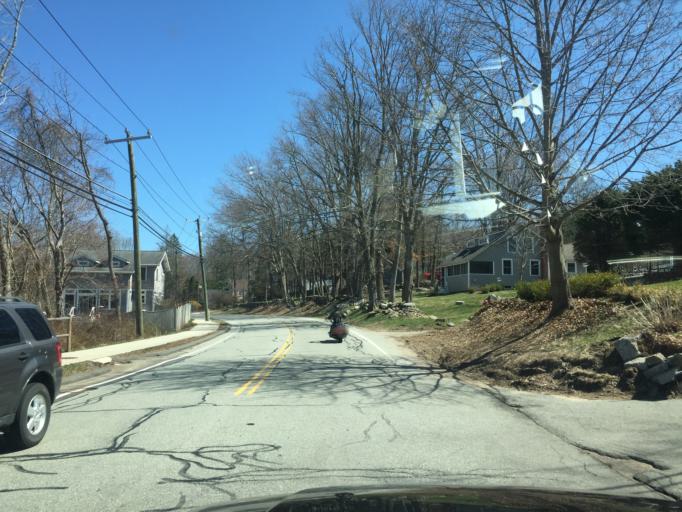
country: US
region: Connecticut
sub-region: Hartford County
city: Terramuggus
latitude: 41.6343
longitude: -72.4690
